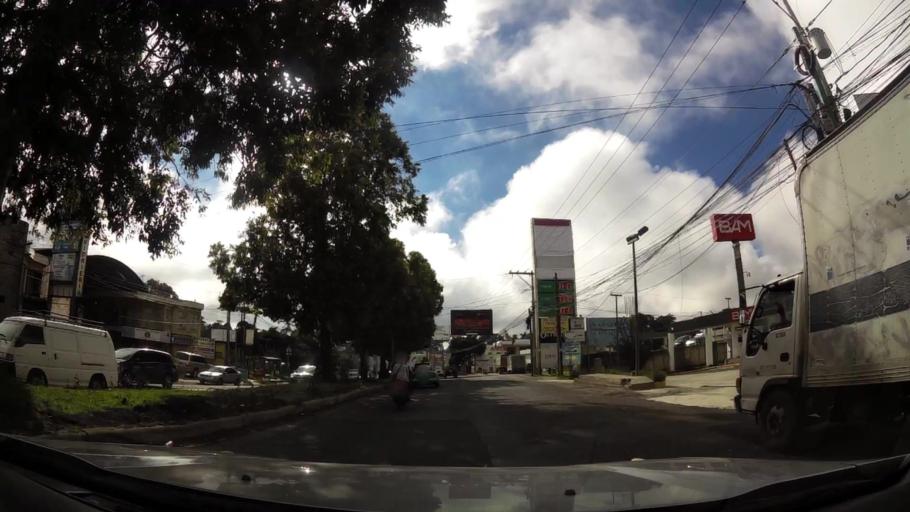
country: GT
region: Guatemala
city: Santa Catarina Pinula
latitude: 14.5608
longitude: -90.4628
